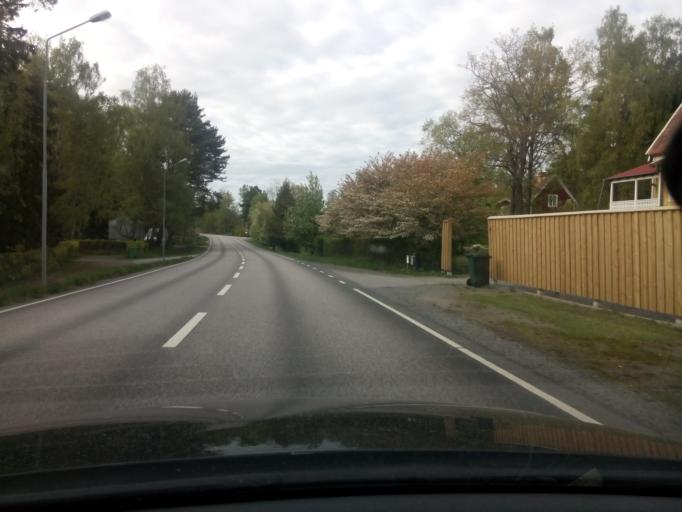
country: SE
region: Soedermanland
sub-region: Flens Kommun
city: Malmkoping
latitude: 59.0709
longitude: 16.8168
